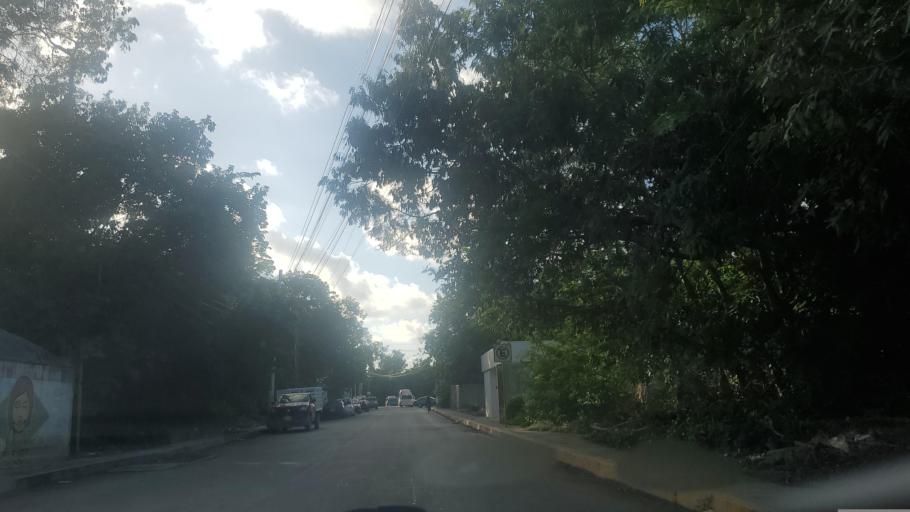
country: MX
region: Quintana Roo
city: Tulum
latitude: 20.2164
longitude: -87.4511
